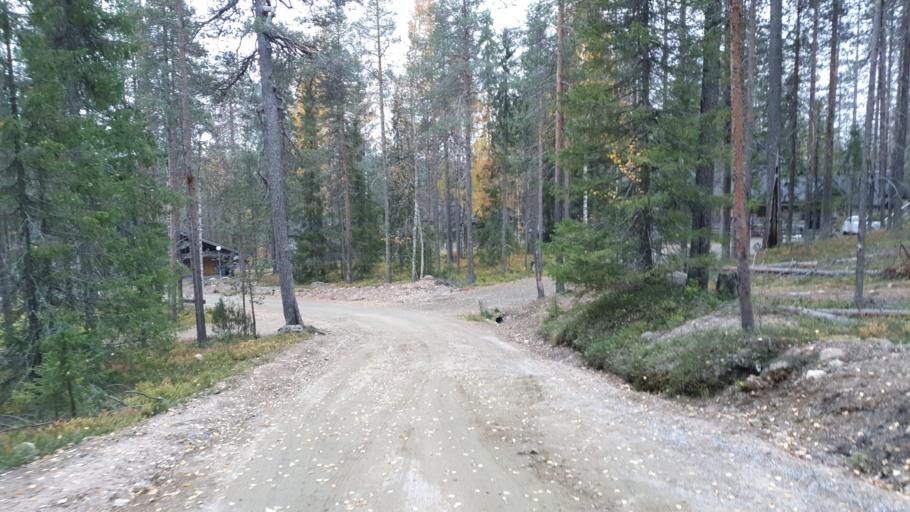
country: FI
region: Lapland
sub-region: Tunturi-Lappi
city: Kolari
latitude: 67.5983
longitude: 24.1138
